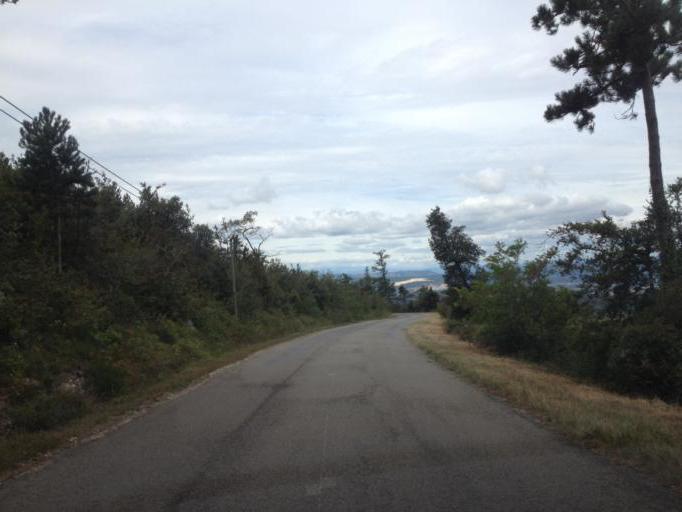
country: FR
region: Rhone-Alpes
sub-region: Departement de la Drome
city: Allan
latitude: 44.4745
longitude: 4.8072
